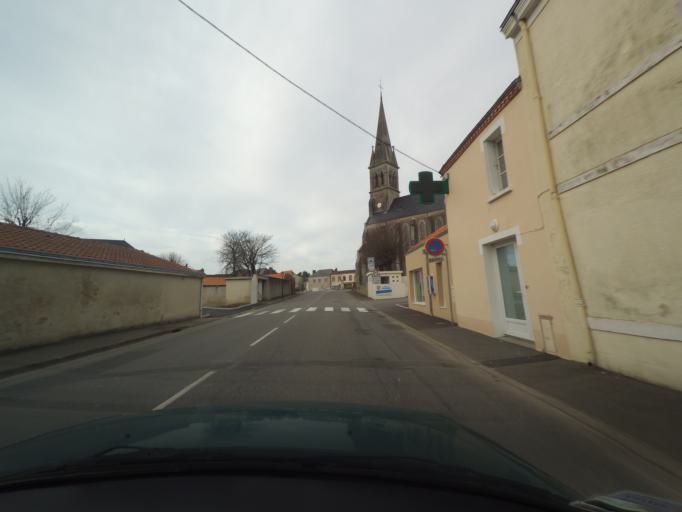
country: FR
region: Pays de la Loire
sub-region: Departement de la Loire-Atlantique
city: Chauve
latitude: 47.1506
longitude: -1.9848
